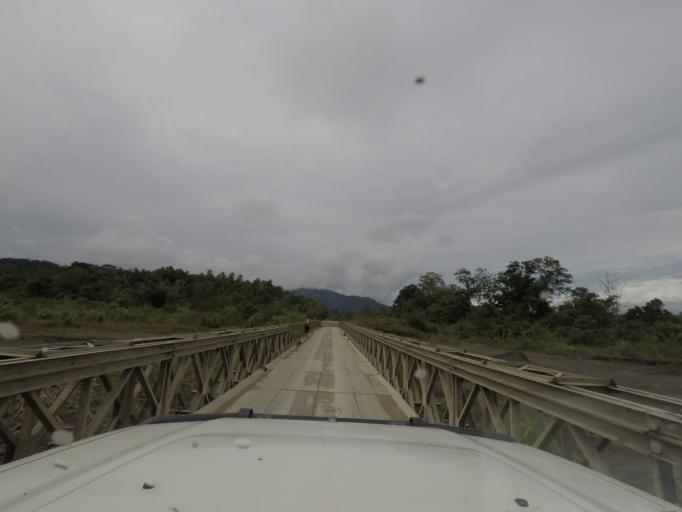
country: PG
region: Madang
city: Madang
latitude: -5.5658
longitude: 145.4315
